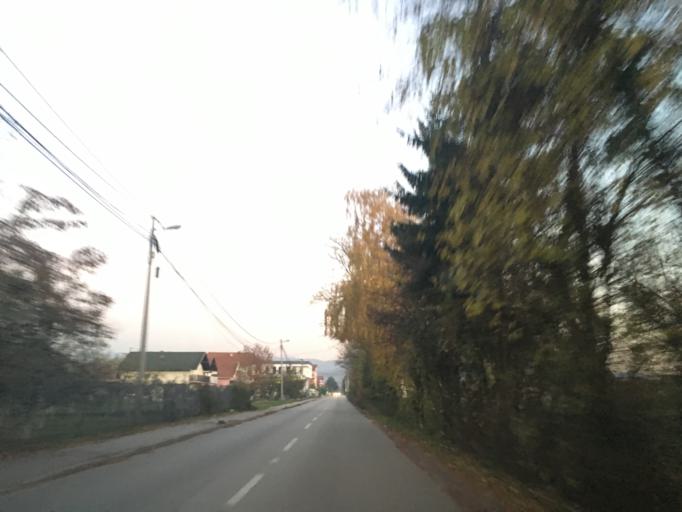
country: BA
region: Federation of Bosnia and Herzegovina
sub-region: Kanton Sarajevo
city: Sarajevo
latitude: 43.8190
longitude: 18.3314
